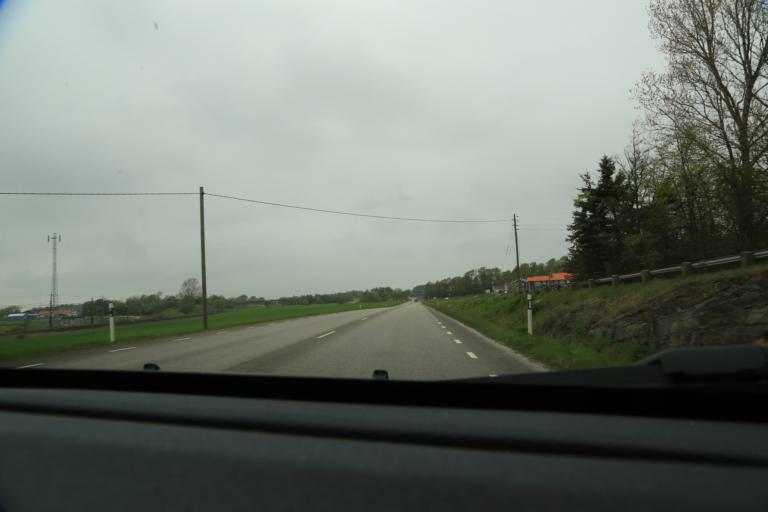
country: SE
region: Halland
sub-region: Kungsbacka Kommun
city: Frillesas
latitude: 57.2376
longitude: 12.1994
